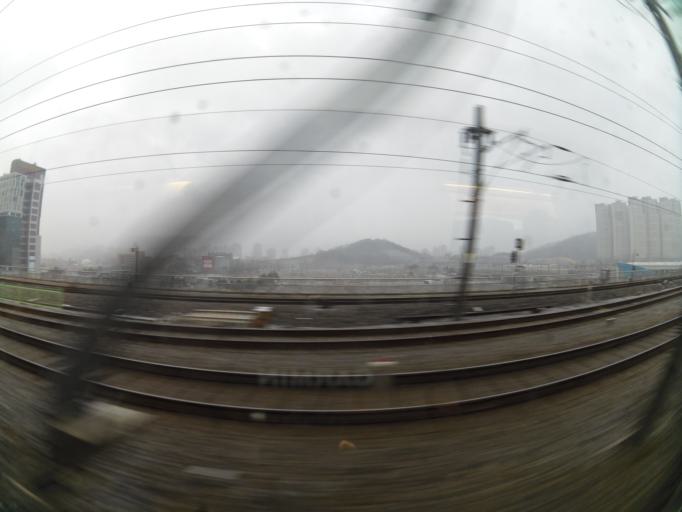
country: KR
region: Chungcheongnam-do
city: Cheonan
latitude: 36.7903
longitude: 127.1054
